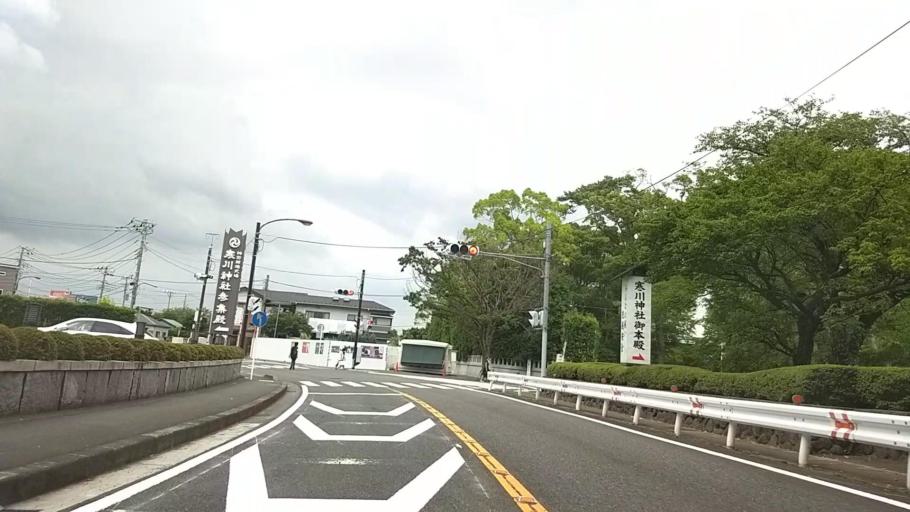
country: JP
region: Kanagawa
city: Chigasaki
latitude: 35.3777
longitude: 139.3812
